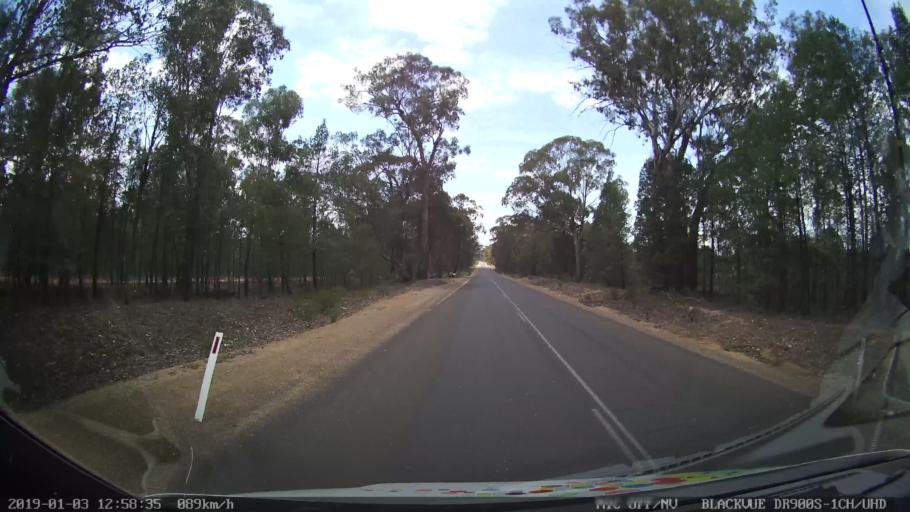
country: AU
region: New South Wales
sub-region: Cabonne
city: Canowindra
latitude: -33.6410
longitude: 148.3771
